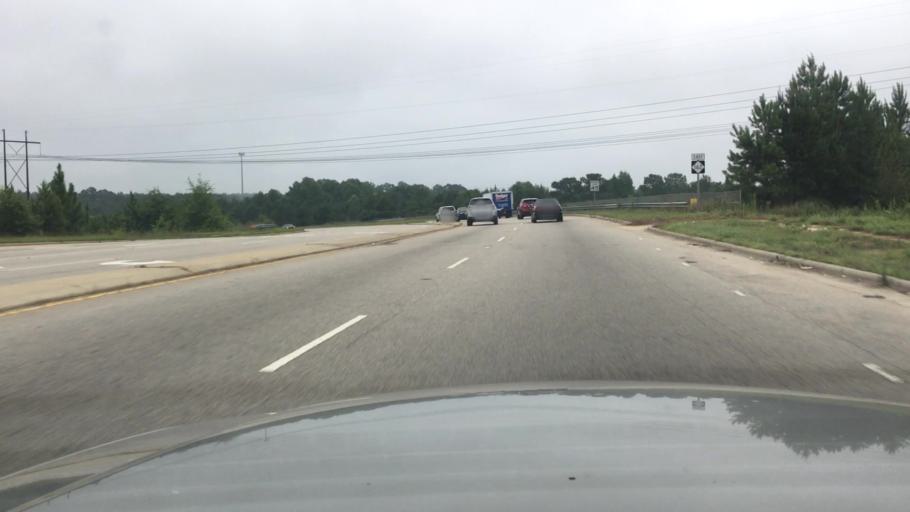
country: US
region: North Carolina
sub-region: Cumberland County
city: Hope Mills
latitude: 34.9906
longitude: -78.9484
